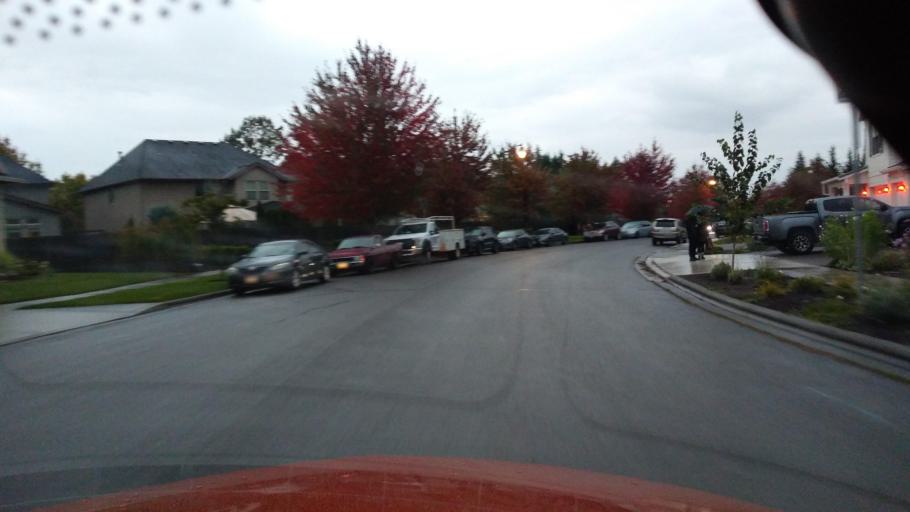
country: US
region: Oregon
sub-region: Washington County
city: Forest Grove
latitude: 45.5253
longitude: -123.1258
